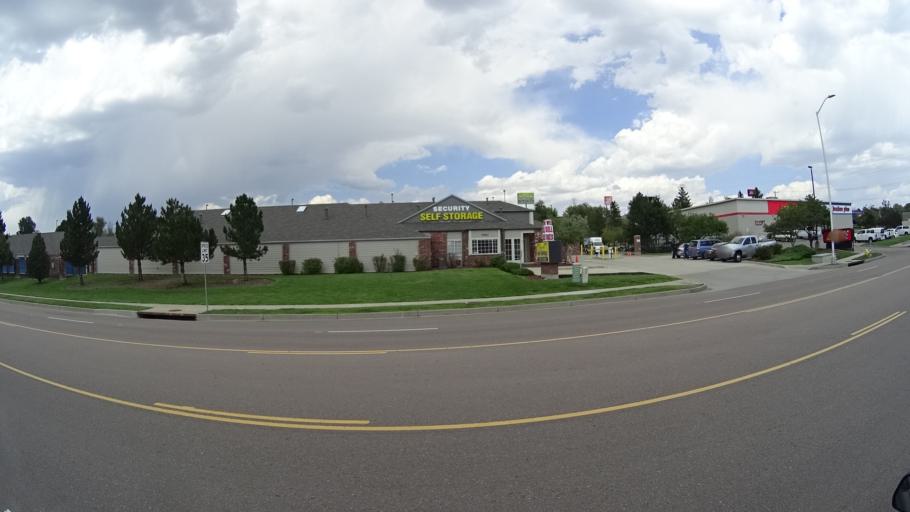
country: US
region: Colorado
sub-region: El Paso County
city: Stratmoor
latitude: 38.8318
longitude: -104.7589
